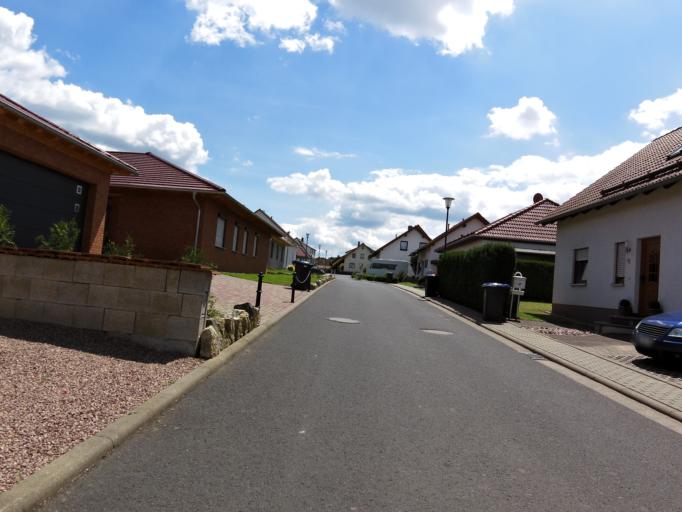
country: DE
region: Thuringia
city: Lauchroden
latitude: 50.9931
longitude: 10.1513
